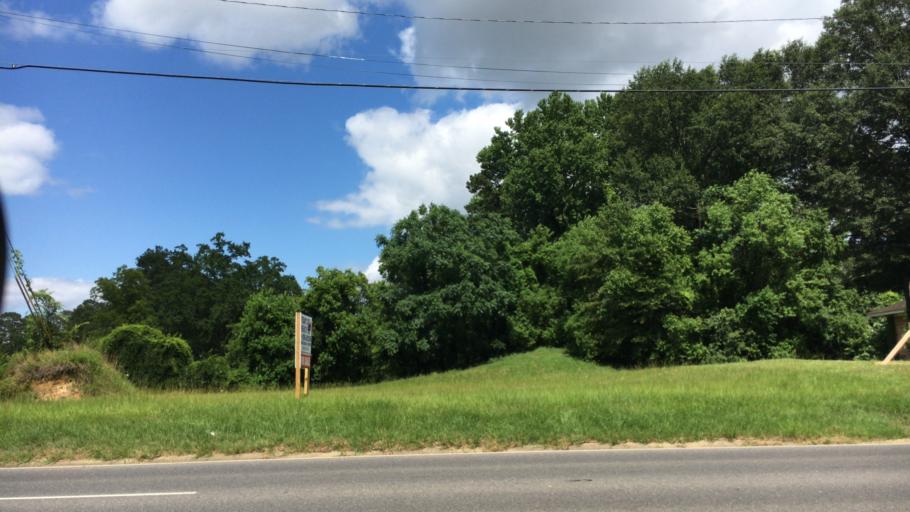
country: US
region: Louisiana
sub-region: Lincoln Parish
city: Ruston
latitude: 32.5474
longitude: -92.6400
